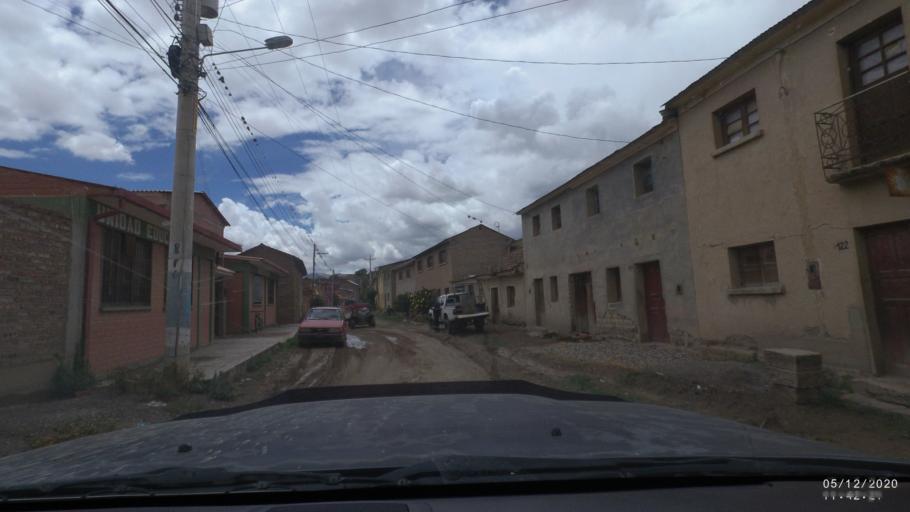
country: BO
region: Cochabamba
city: Sipe Sipe
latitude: -17.5538
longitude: -66.3419
